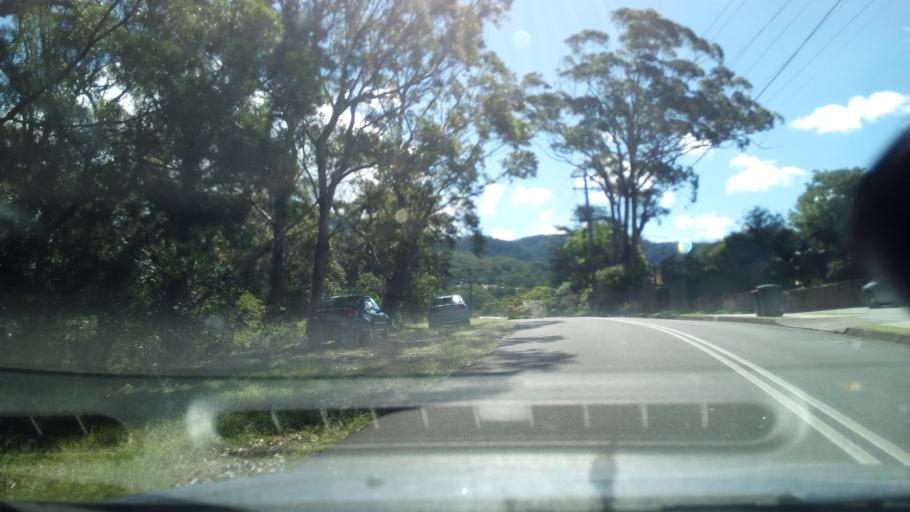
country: AU
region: New South Wales
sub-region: Wollongong
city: Mount Ousley
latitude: -34.4008
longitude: 150.8816
